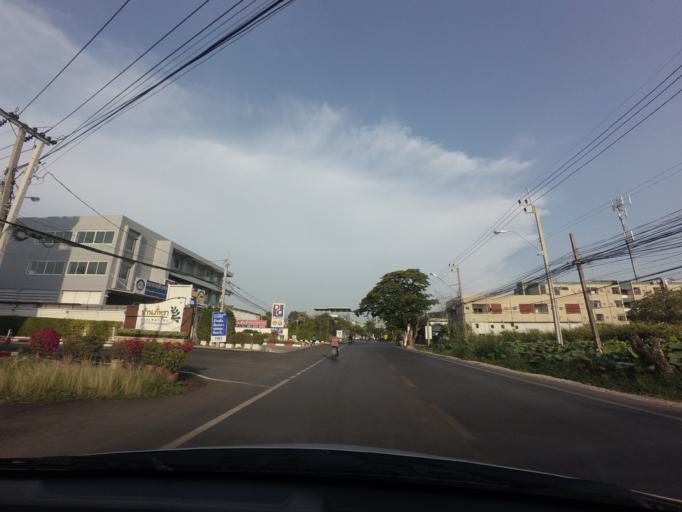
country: TH
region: Bangkok
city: Saphan Sung
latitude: 13.7394
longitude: 100.6914
